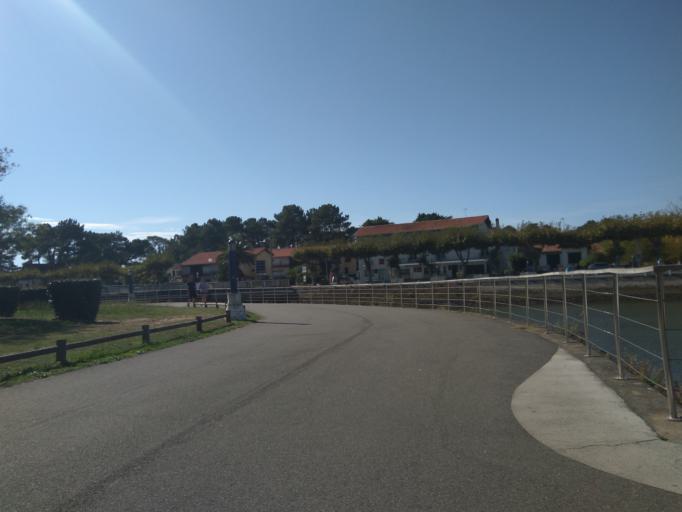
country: FR
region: Aquitaine
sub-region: Departement des Landes
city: Capbreton
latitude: 43.6494
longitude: -1.4349
